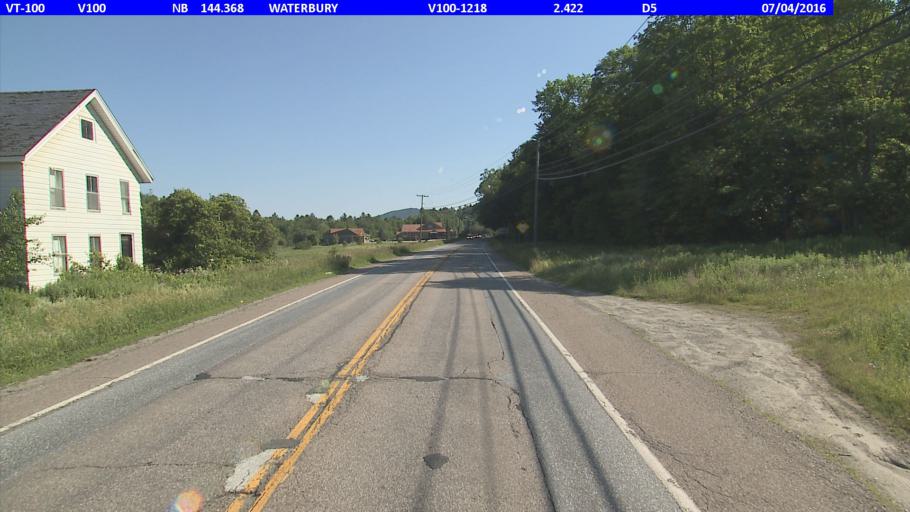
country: US
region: Vermont
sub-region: Washington County
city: Waterbury
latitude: 44.3664
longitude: -72.7301
